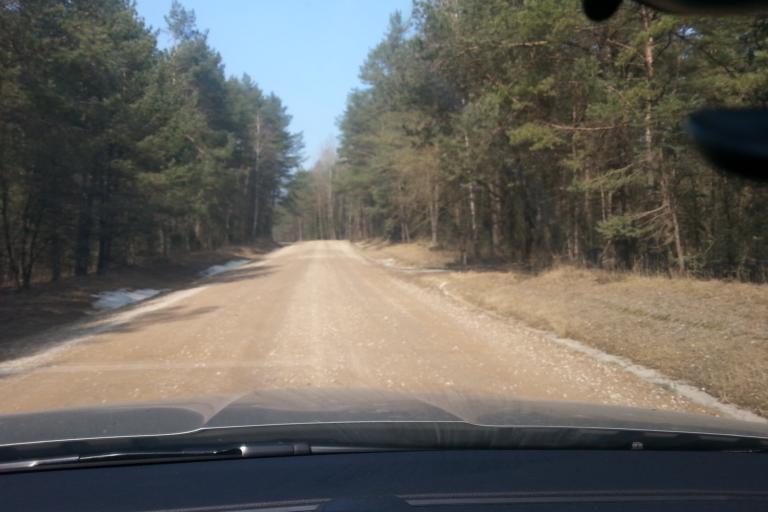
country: LT
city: Trakai
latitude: 54.5624
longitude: 24.9776
